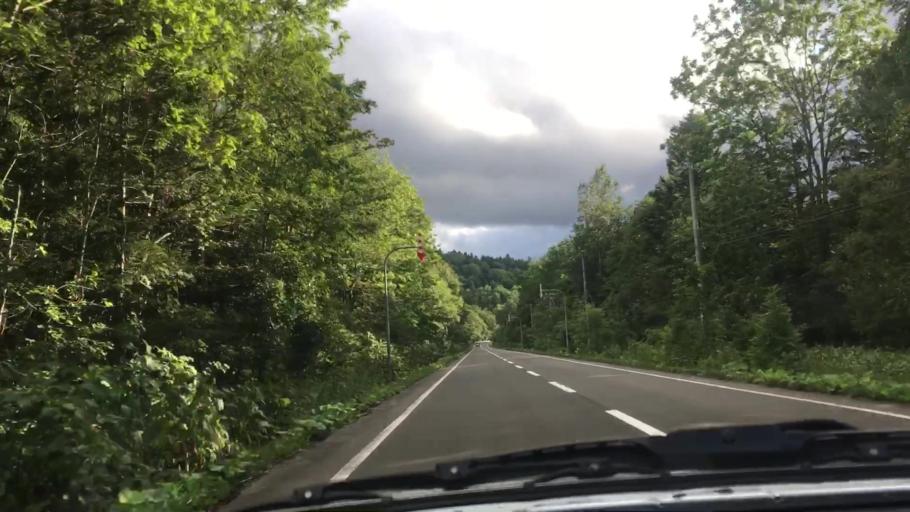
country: JP
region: Hokkaido
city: Shimo-furano
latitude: 43.0905
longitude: 142.6819
